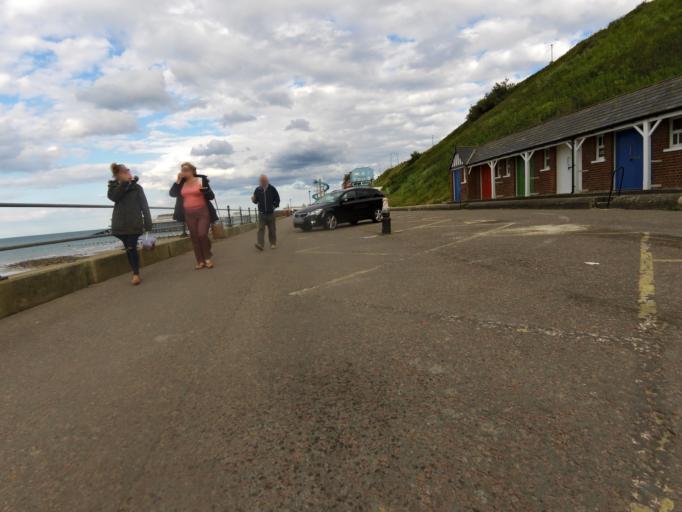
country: GB
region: England
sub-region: Norfolk
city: Cromer
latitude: 52.9335
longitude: 1.2959
